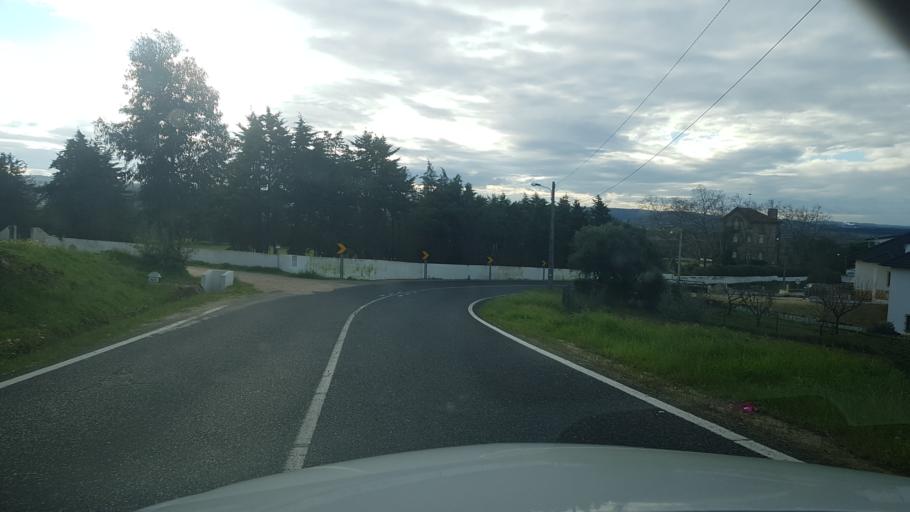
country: PT
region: Santarem
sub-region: Abrantes
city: Tramagal
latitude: 39.4742
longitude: -8.2368
